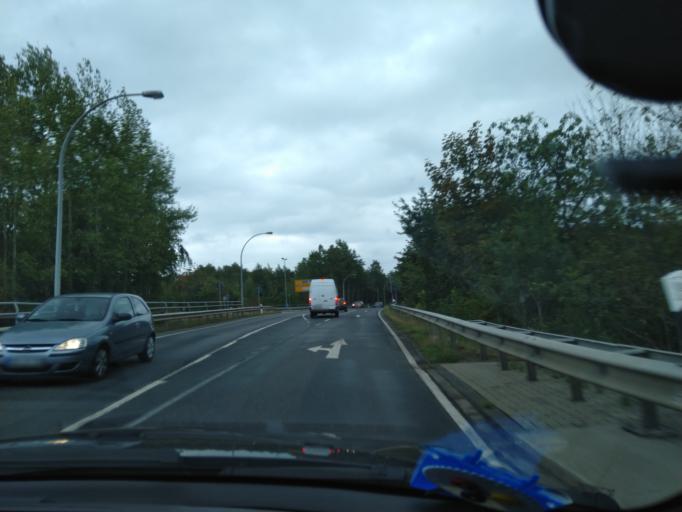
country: DE
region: Lower Saxony
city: Nordhorn
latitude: 52.4209
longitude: 7.0876
